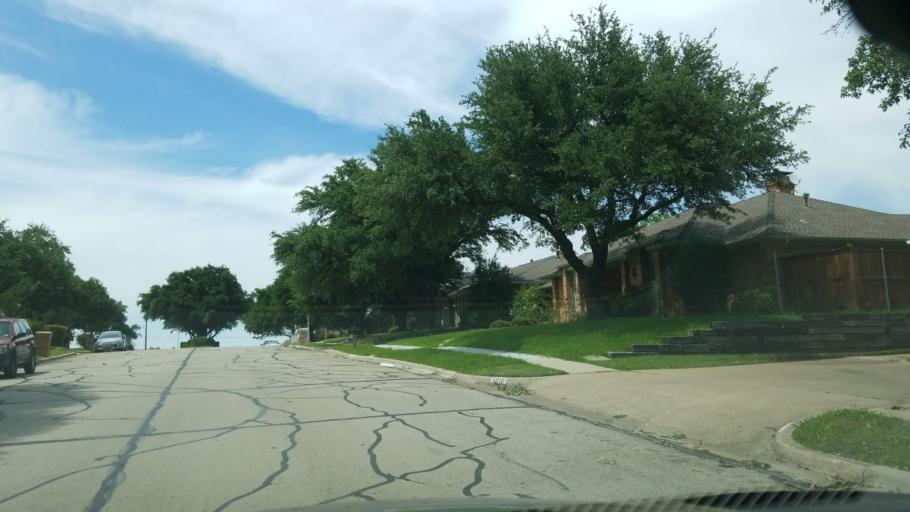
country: US
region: Texas
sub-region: Dallas County
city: Irving
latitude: 32.8765
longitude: -96.9980
